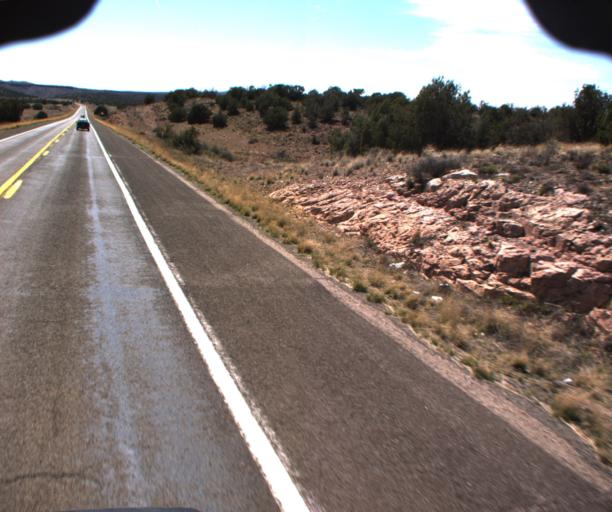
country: US
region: Arizona
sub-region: Mohave County
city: Peach Springs
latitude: 35.4583
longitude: -113.6181
